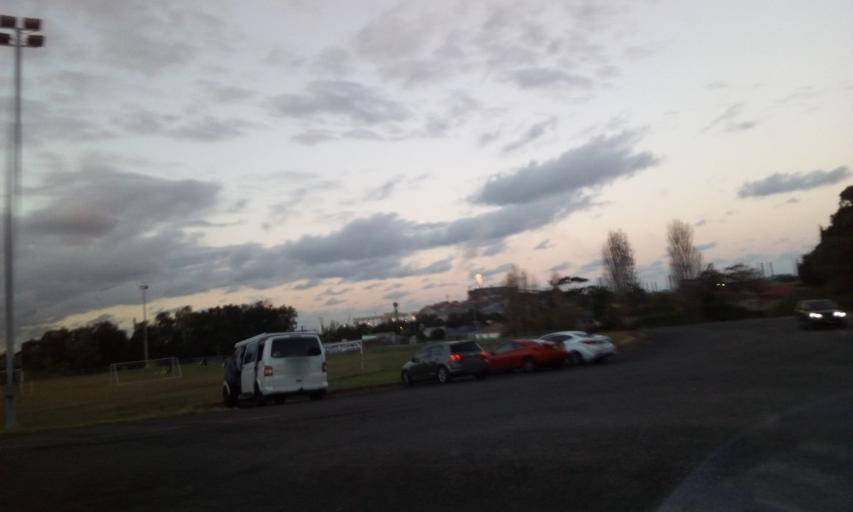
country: AU
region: New South Wales
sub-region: Wollongong
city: Cringila
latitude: -34.4675
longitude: 150.8685
